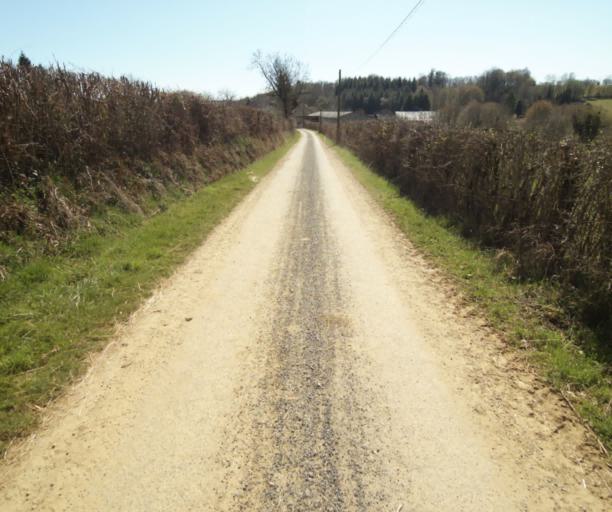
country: FR
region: Limousin
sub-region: Departement de la Correze
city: Chamboulive
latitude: 45.4628
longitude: 1.6681
